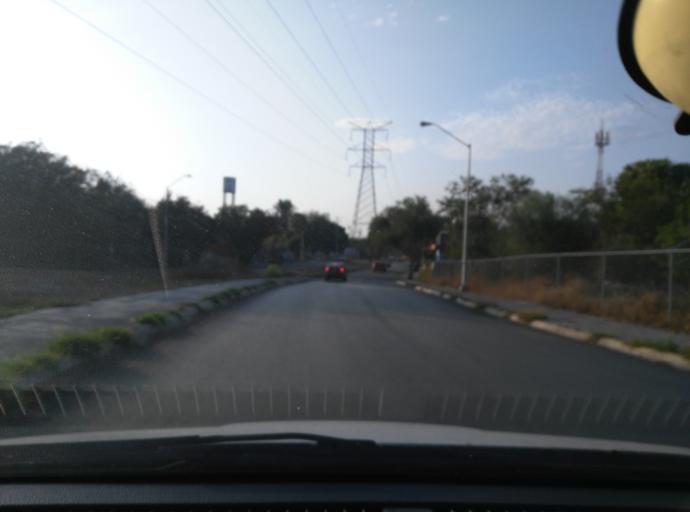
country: MX
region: Nuevo Leon
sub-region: San Nicolas de los Garza
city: San Nicolas de los Garza
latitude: 25.7587
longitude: -100.2508
